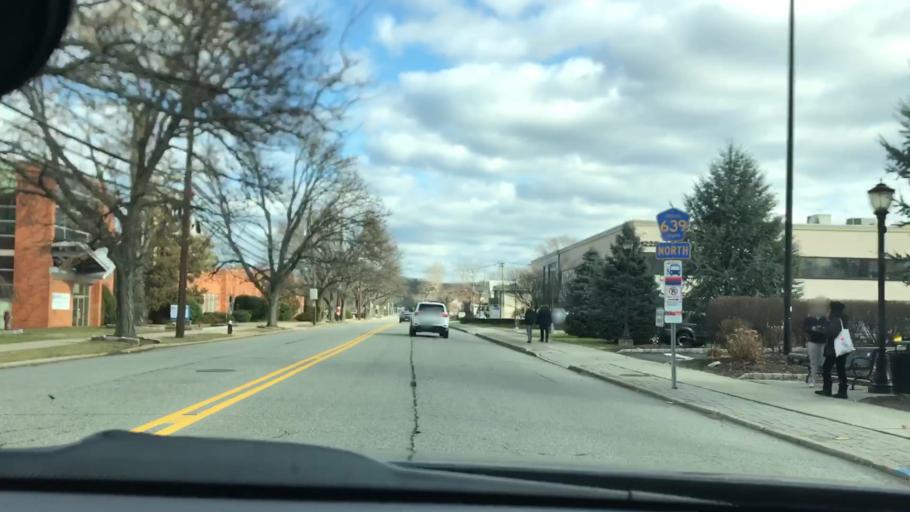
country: US
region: New Jersey
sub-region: Passaic County
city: Totowa
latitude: 40.8909
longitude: -74.2147
